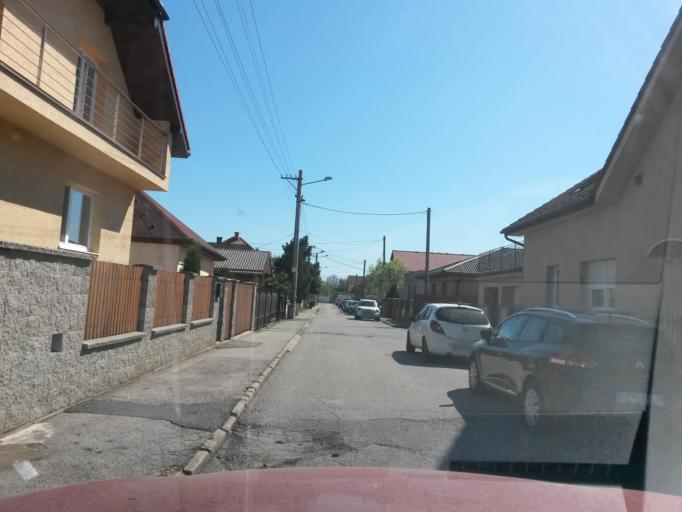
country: SK
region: Kosicky
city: Kosice
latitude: 48.6796
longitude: 21.2722
